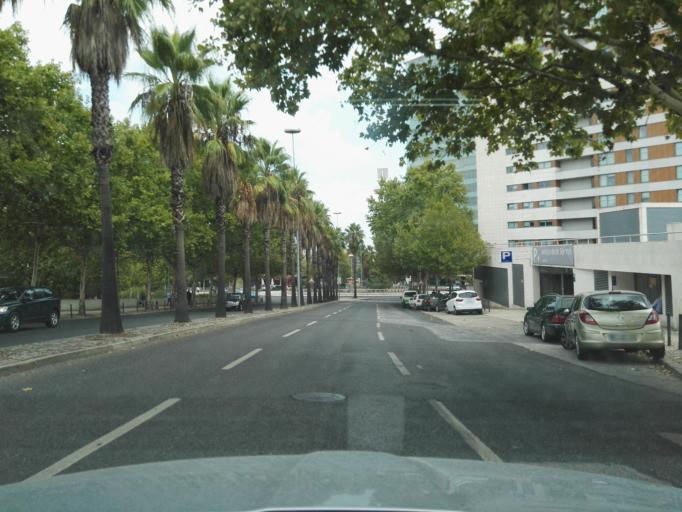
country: PT
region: Lisbon
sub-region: Loures
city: Moscavide
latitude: 38.7751
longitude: -9.0988
